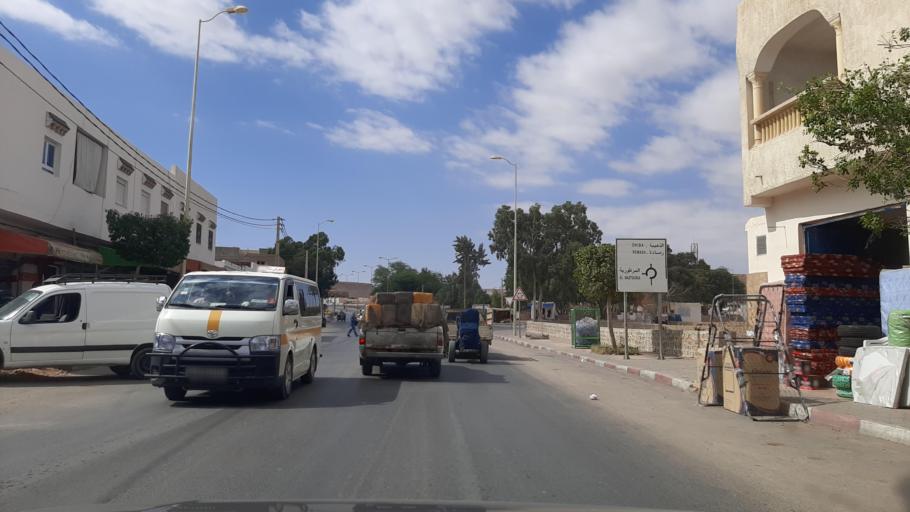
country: TN
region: Tataouine
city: Tataouine
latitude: 32.9257
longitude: 10.4409
